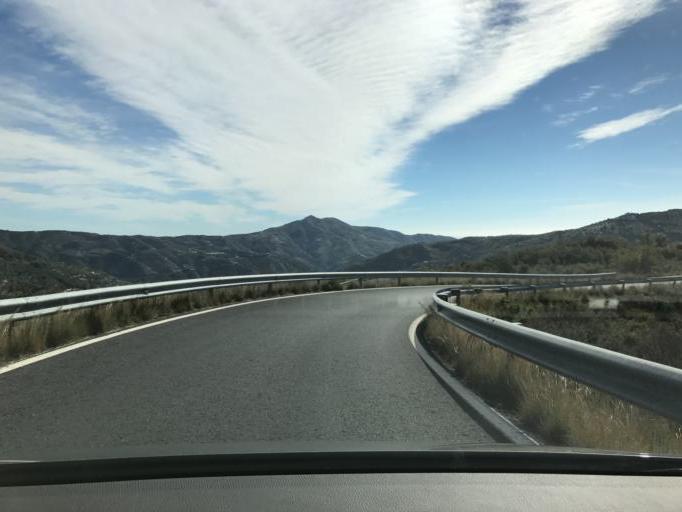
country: ES
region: Andalusia
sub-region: Provincia de Granada
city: Otivar
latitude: 36.8217
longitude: -3.6952
